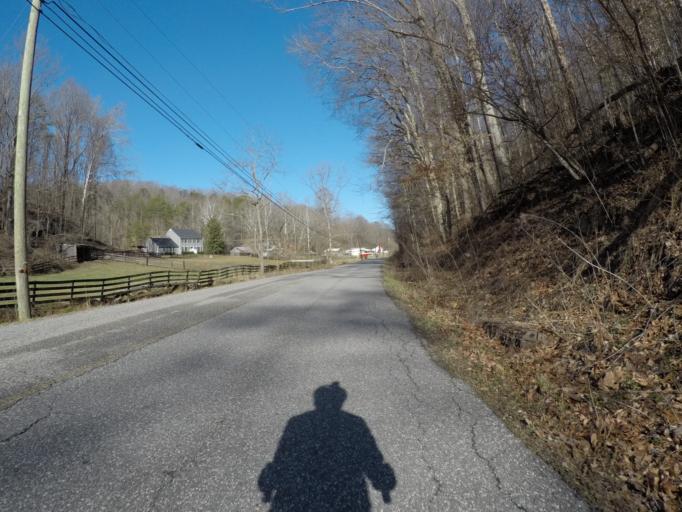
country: US
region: Kentucky
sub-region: Boyd County
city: Catlettsburg
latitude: 38.4231
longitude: -82.6378
